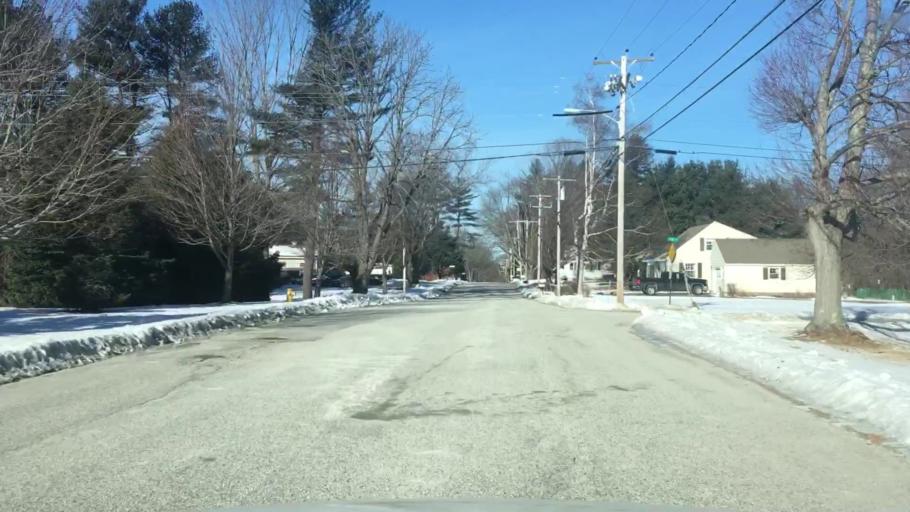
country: US
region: Maine
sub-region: Cumberland County
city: South Windham
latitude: 43.7313
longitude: -70.4182
